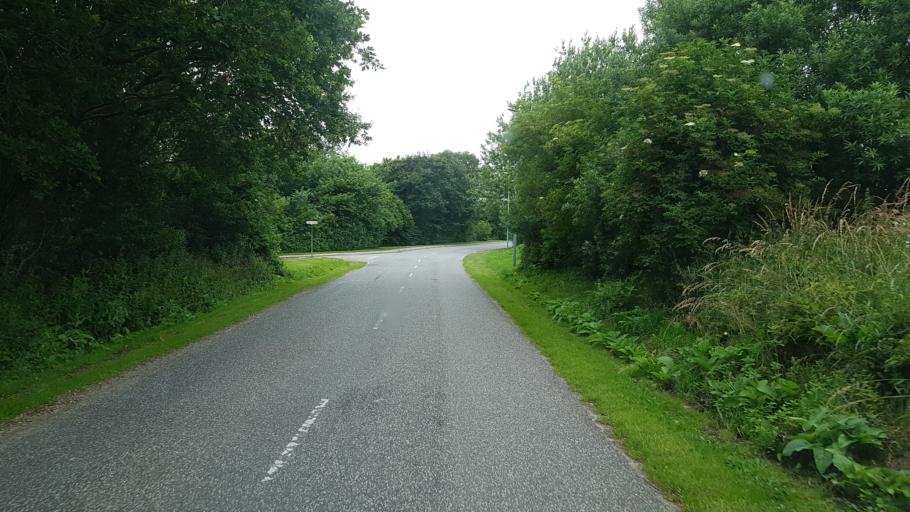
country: DK
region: Central Jutland
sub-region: Lemvig Kommune
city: Lemvig
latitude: 56.5464
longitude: 8.3273
